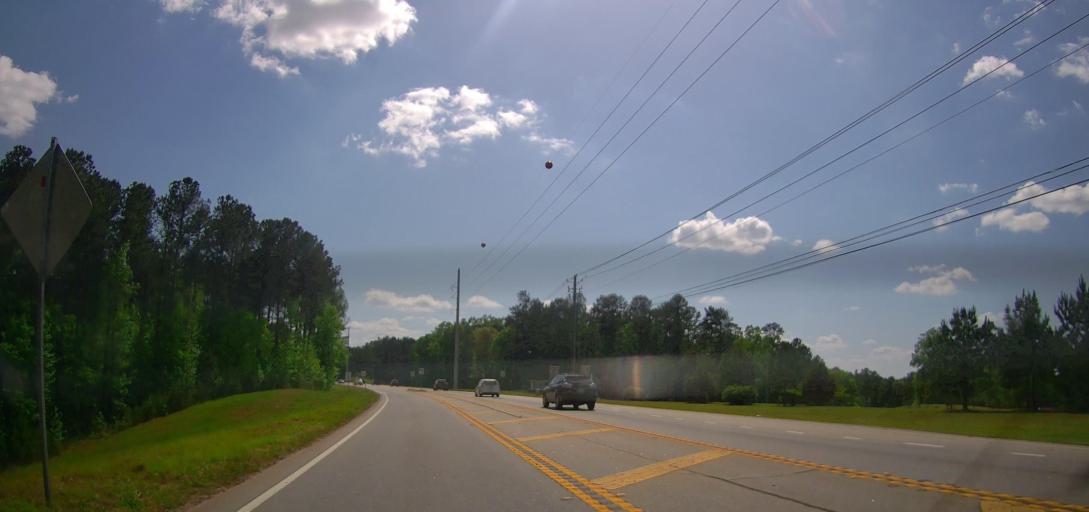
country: US
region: Georgia
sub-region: Putnam County
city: Jefferson
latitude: 33.4805
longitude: -83.2409
